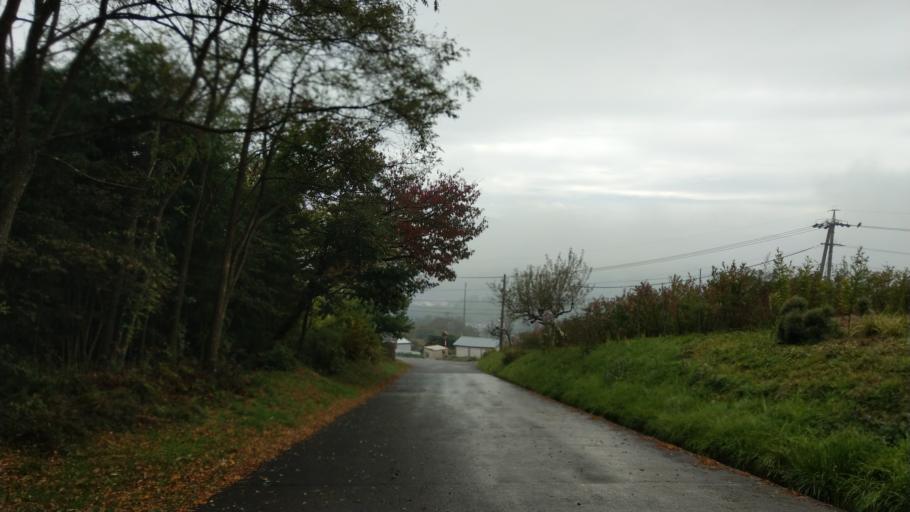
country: JP
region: Nagano
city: Komoro
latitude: 36.3560
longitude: 138.4240
